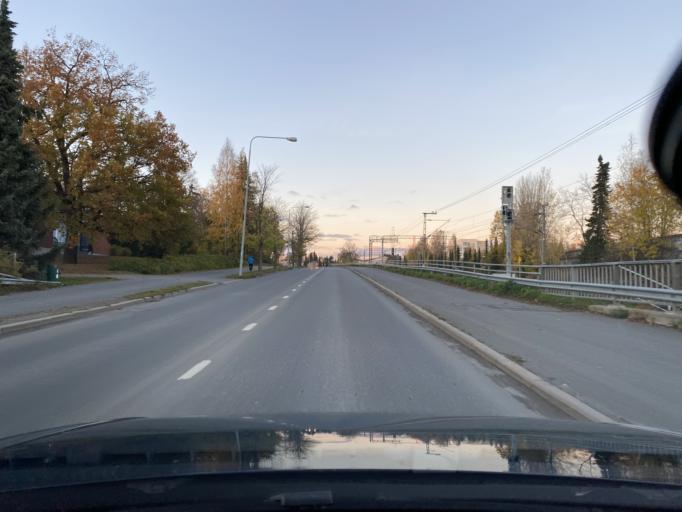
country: FI
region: Pirkanmaa
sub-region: Tampere
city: Lempaeaelae
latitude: 61.3089
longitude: 23.7527
